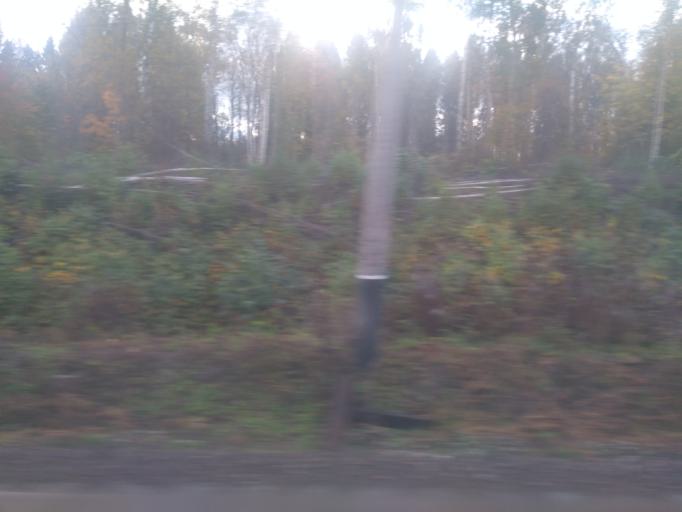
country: RU
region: Udmurtiya
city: Mozhga
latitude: 56.4264
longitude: 52.0478
